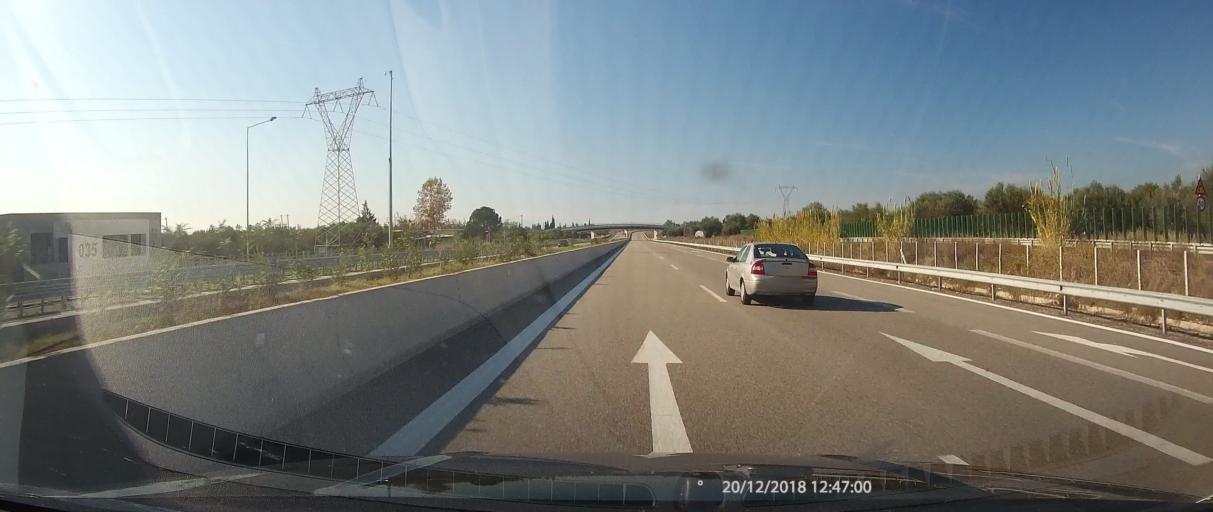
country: GR
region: West Greece
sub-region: Nomos Aitolias kai Akarnanias
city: Mesolongi
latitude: 38.3923
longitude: 21.4587
